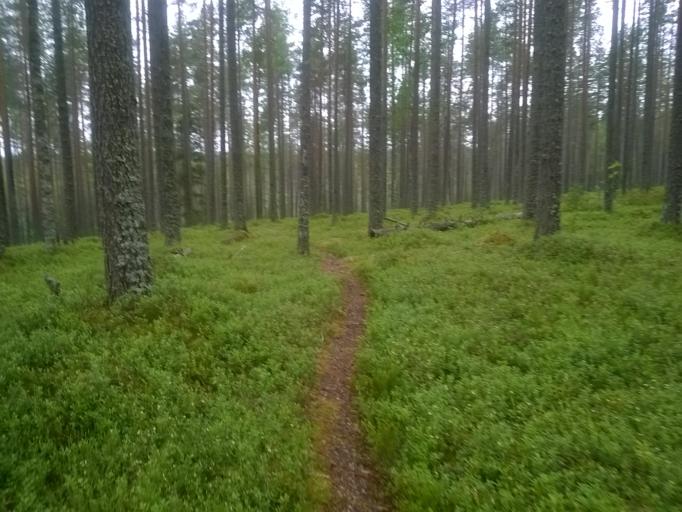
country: RU
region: Republic of Karelia
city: Kostomuksha
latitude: 64.3243
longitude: 30.0815
